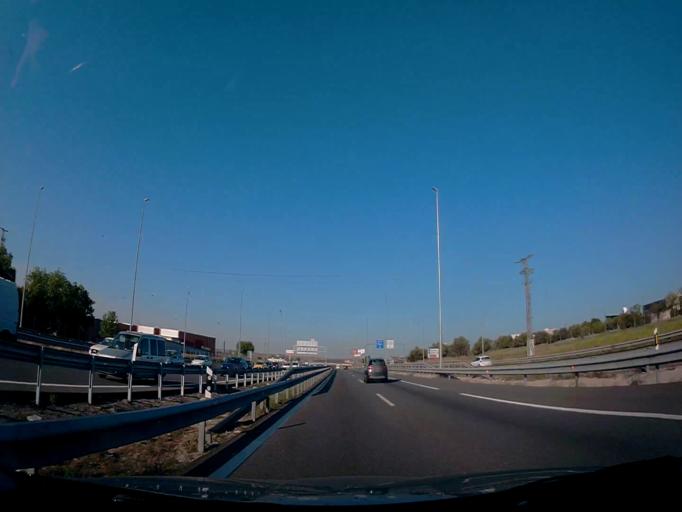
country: ES
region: Madrid
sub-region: Provincia de Madrid
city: Mostoles
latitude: 40.3364
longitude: -3.8829
